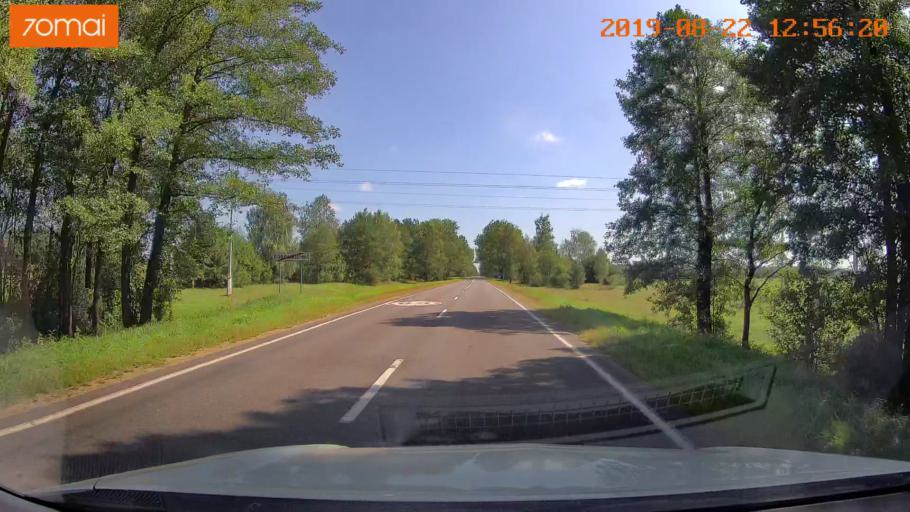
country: BY
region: Minsk
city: Prawdzinski
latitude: 53.4333
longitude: 27.7291
